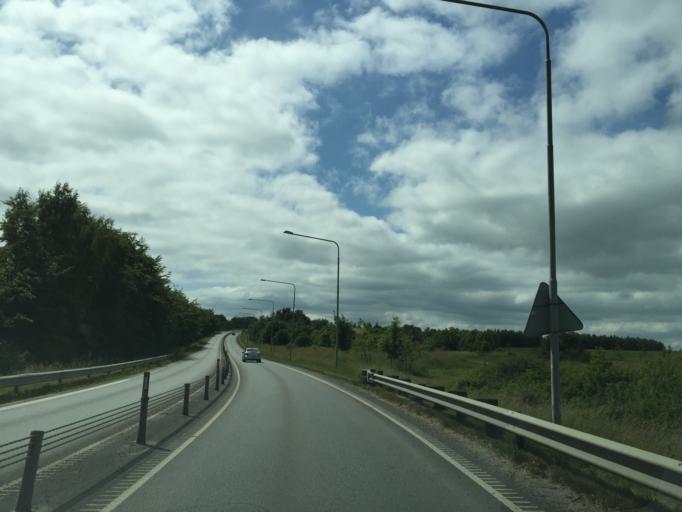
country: SE
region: Skane
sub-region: Ystads Kommun
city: Ystad
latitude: 55.4439
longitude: 13.8317
